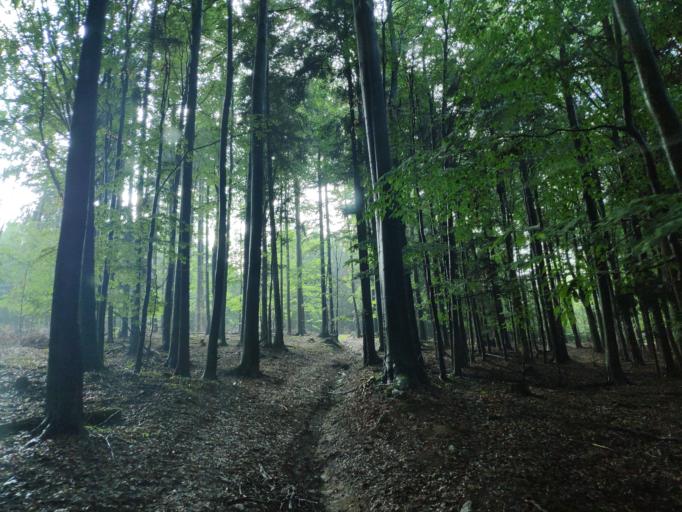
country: SK
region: Kosicky
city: Medzev
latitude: 48.7495
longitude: 20.9918
